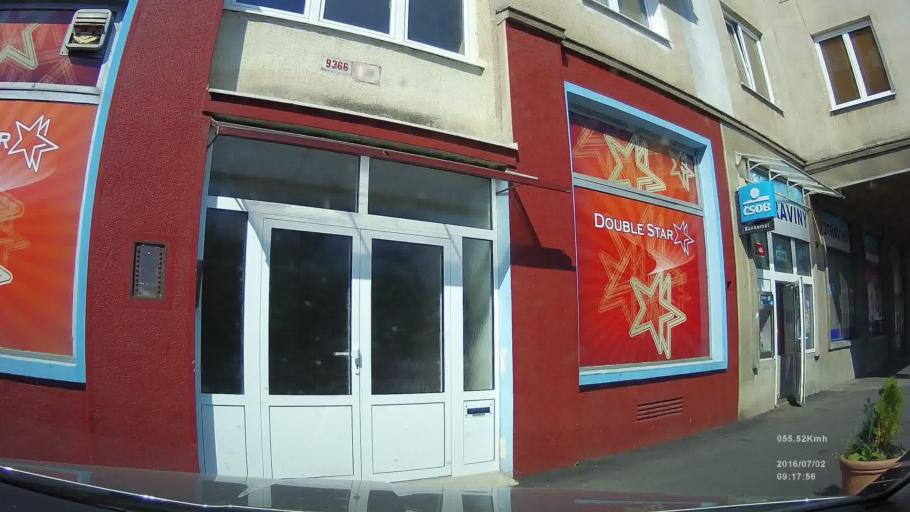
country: SK
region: Kosicky
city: Kosice
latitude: 48.7335
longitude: 21.2343
